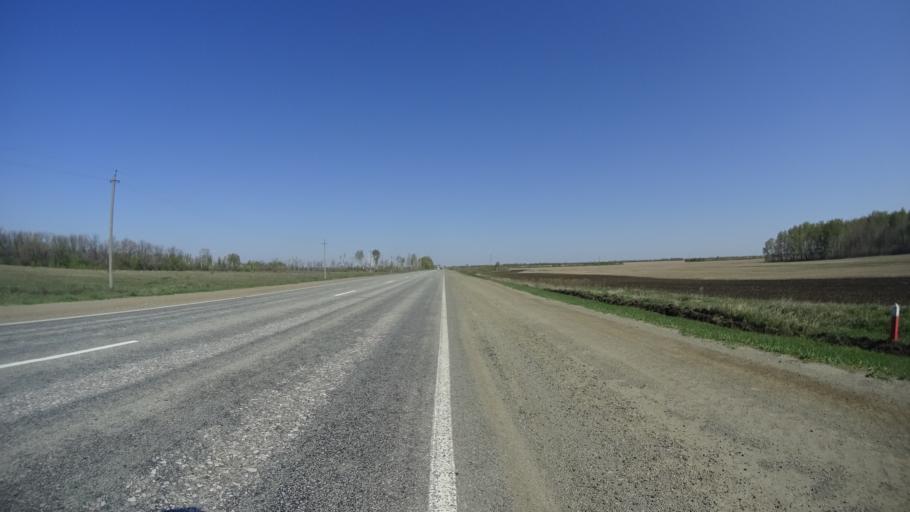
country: RU
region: Chelyabinsk
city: Troitsk
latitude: 54.1925
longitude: 61.4332
